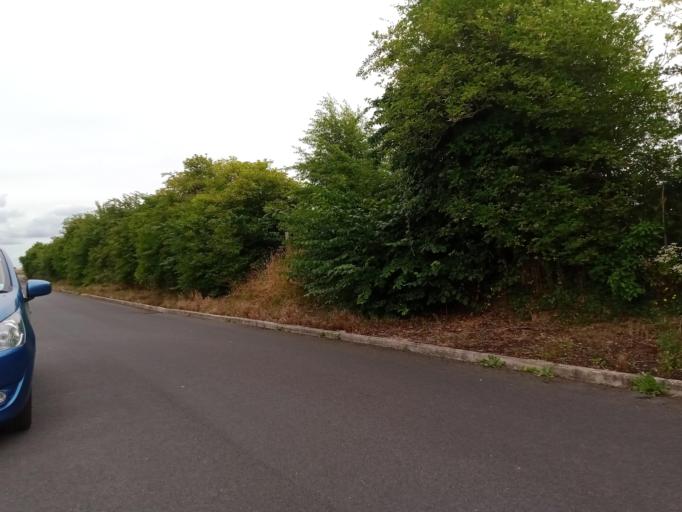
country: IE
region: Leinster
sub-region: Kilkenny
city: Callan
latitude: 52.5479
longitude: -7.3833
